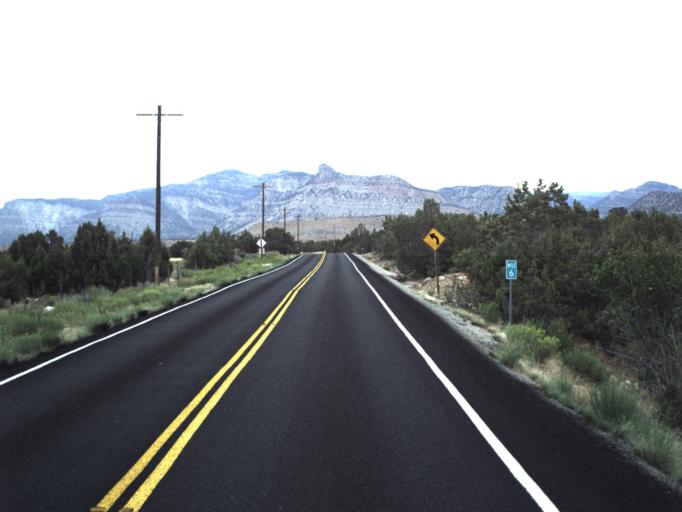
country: US
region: Utah
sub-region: Carbon County
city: East Carbon City
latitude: 39.5226
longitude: -110.3985
